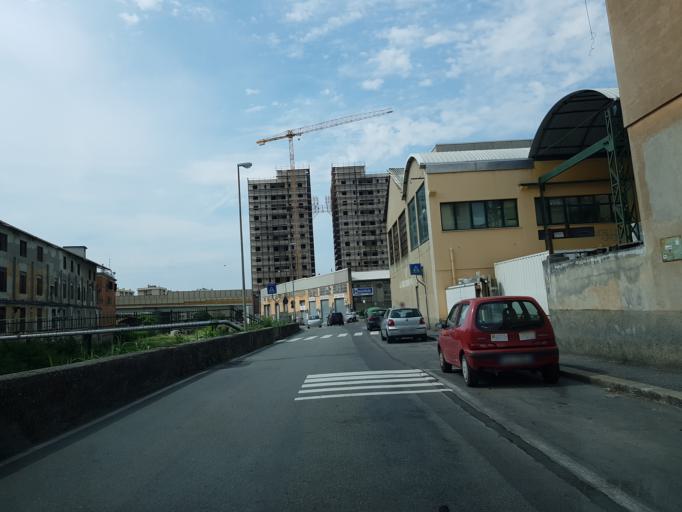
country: IT
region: Liguria
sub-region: Provincia di Genova
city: San Teodoro
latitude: 44.4320
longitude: 8.8545
